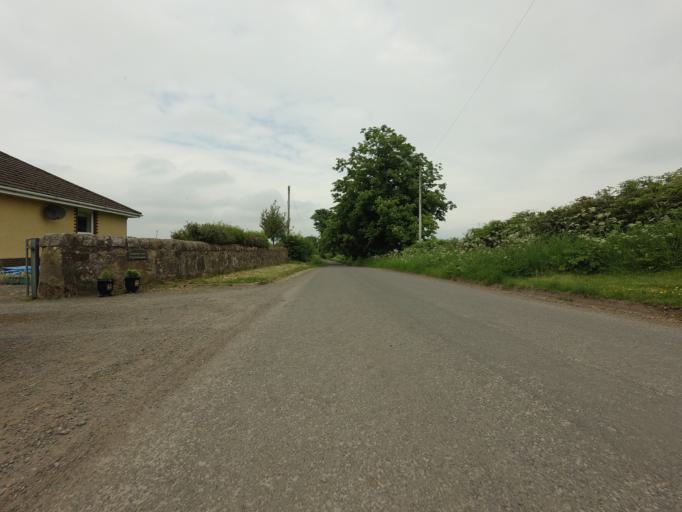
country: GB
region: Scotland
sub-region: Perth and Kinross
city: Kinross
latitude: 56.1839
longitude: -3.4362
